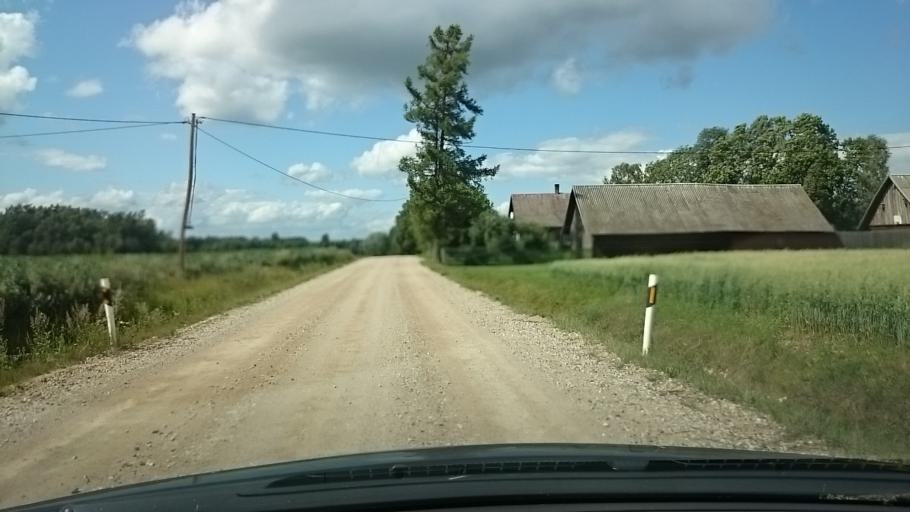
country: EE
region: Polvamaa
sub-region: Polva linn
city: Polva
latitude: 57.9619
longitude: 27.0457
